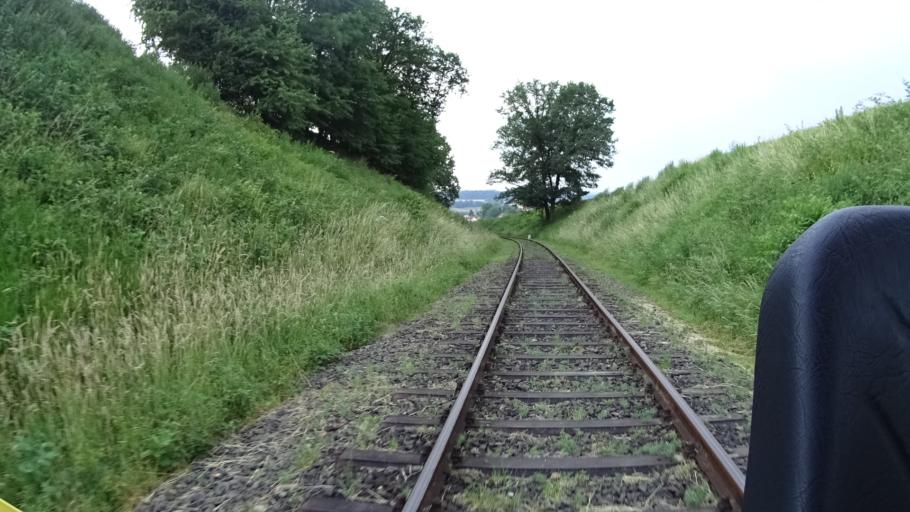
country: DE
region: Hesse
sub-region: Regierungsbezirk Darmstadt
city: Morlenbach
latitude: 49.5916
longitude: 8.7435
